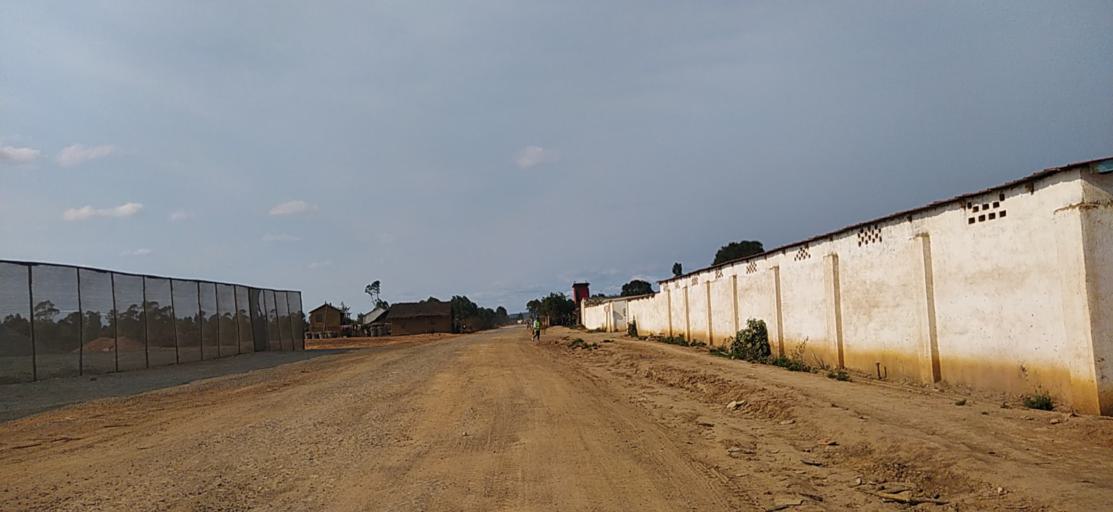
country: MG
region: Alaotra Mangoro
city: Moramanga
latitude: -18.6741
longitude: 48.2733
